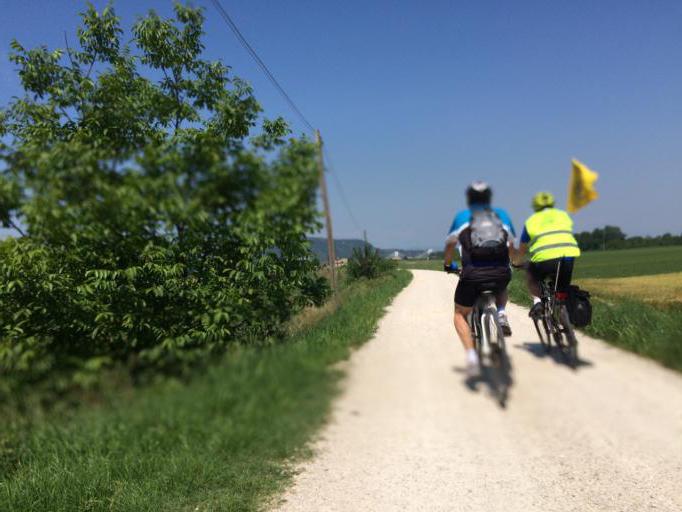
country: IT
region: Veneto
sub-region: Provincia di Vicenza
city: Montegaldella
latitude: 45.4477
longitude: 11.6553
